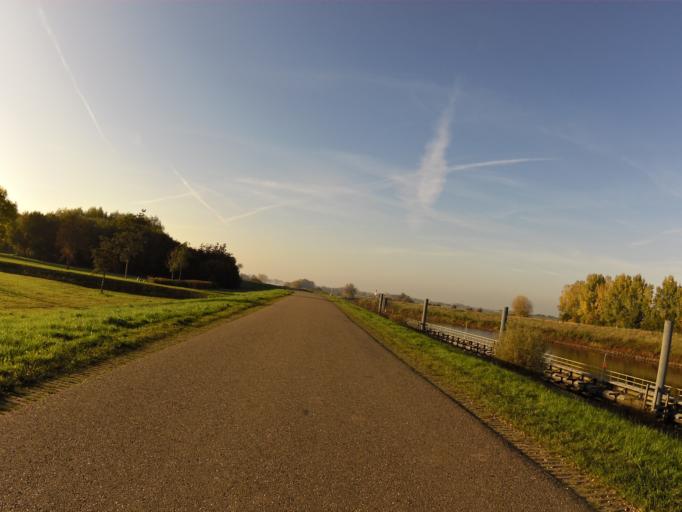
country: NL
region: Gelderland
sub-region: Gemeente Maasdriel
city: Hedel
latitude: 51.7310
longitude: 5.2552
